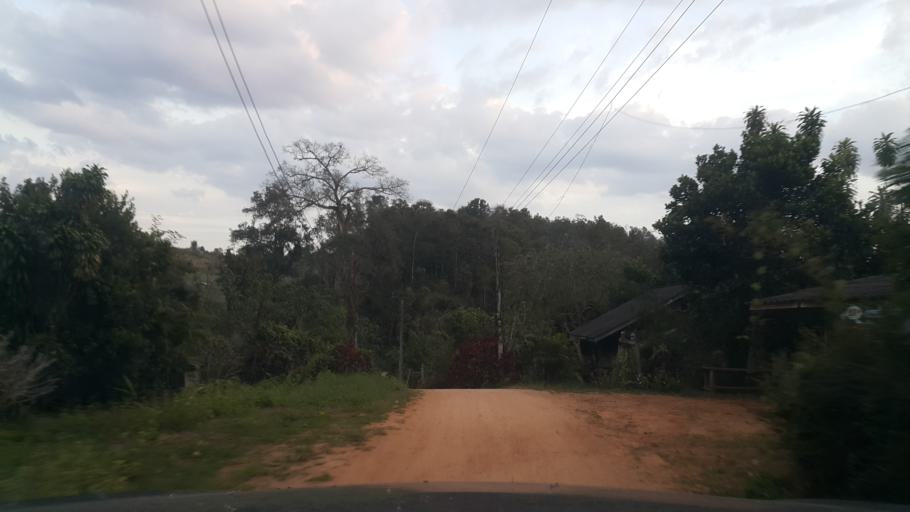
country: TH
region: Chiang Mai
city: Samoeng
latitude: 18.9554
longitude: 98.6749
